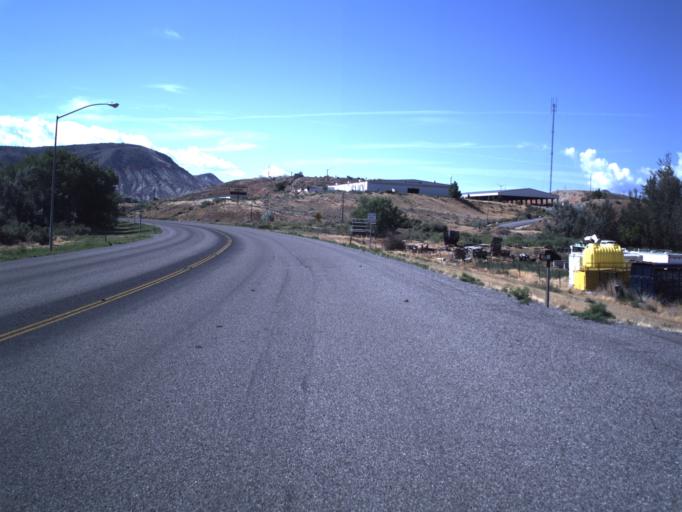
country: US
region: Utah
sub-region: Sevier County
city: Salina
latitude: 38.9515
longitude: -111.8600
